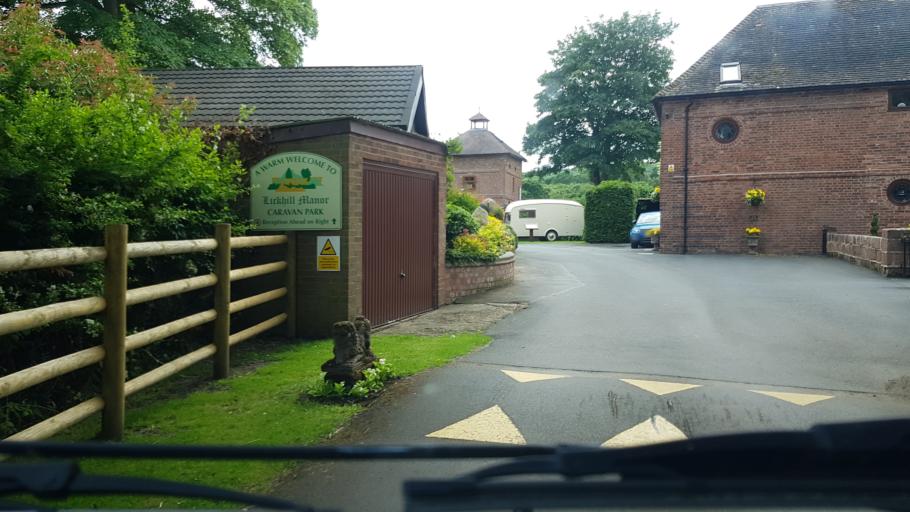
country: GB
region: England
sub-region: Worcestershire
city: Stourport-on-Severn
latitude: 52.3440
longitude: -2.2988
